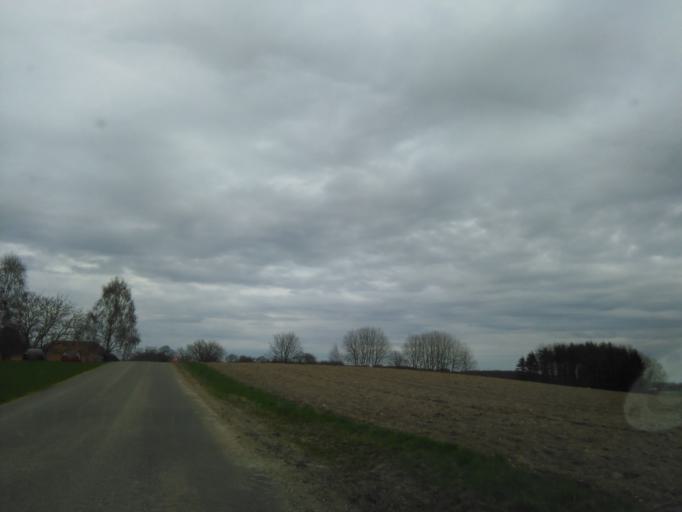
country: DK
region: Central Jutland
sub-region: Skanderborg Kommune
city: Stilling
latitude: 56.0778
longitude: 9.9966
